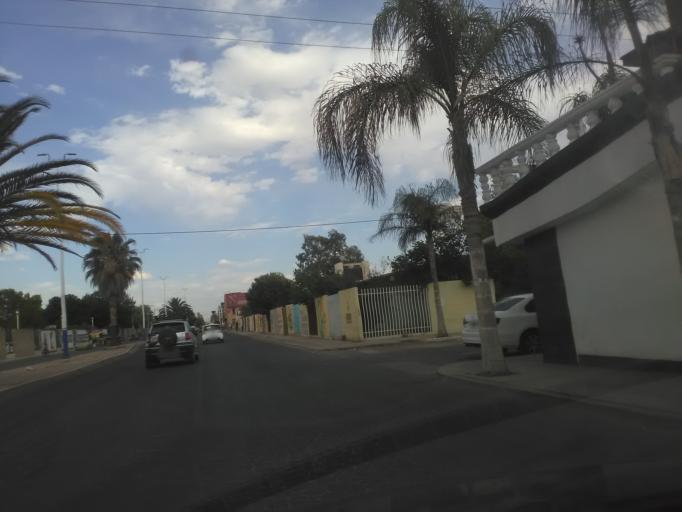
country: MX
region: Durango
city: Victoria de Durango
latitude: 24.0199
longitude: -104.6383
